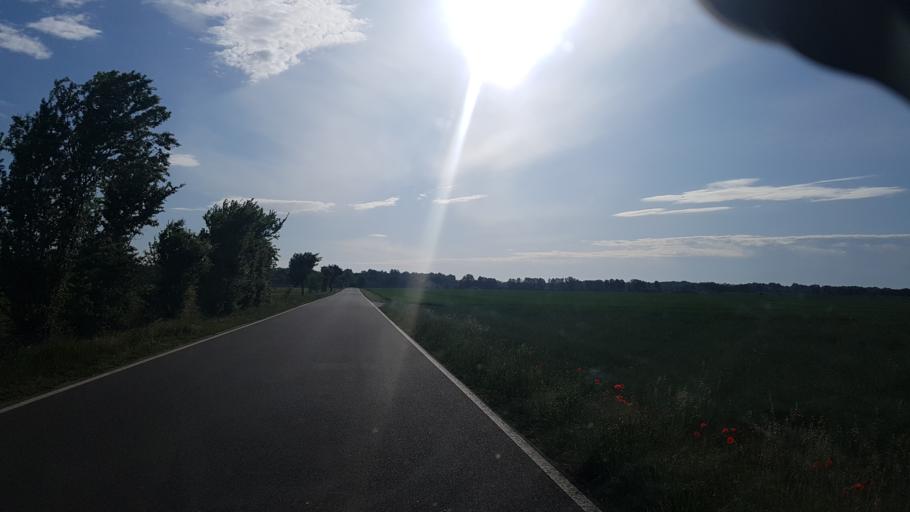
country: DE
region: Brandenburg
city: Luckau
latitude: 51.8239
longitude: 13.7197
